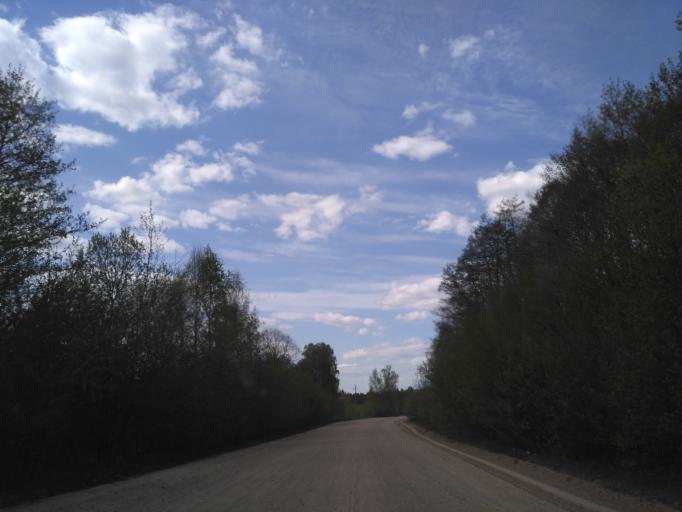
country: BY
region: Minsk
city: Narach
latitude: 54.9996
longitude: 26.5552
